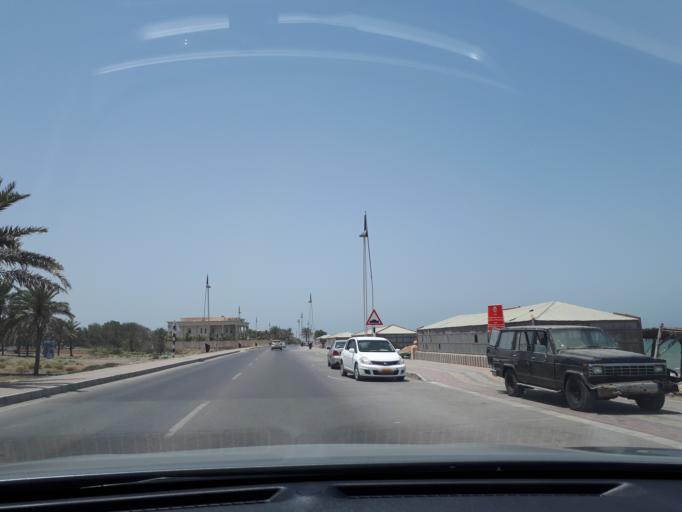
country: OM
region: Muhafazat Masqat
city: As Sib al Jadidah
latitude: 23.6660
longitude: 58.2138
